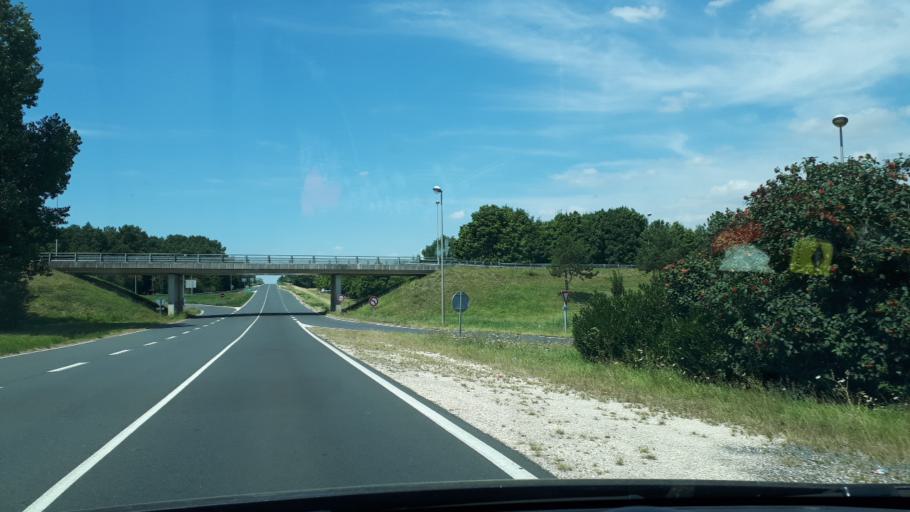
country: FR
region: Centre
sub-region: Departement du Loir-et-Cher
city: Naveil
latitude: 47.8125
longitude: 1.0233
